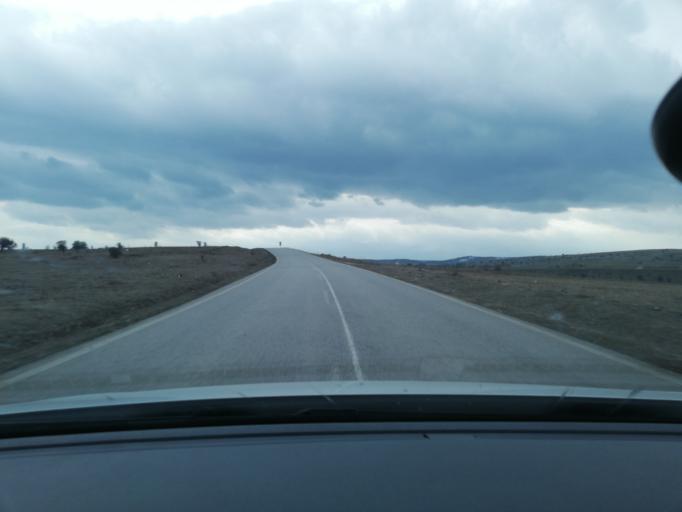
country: TR
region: Bolu
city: Gerede
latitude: 40.7128
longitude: 32.2252
